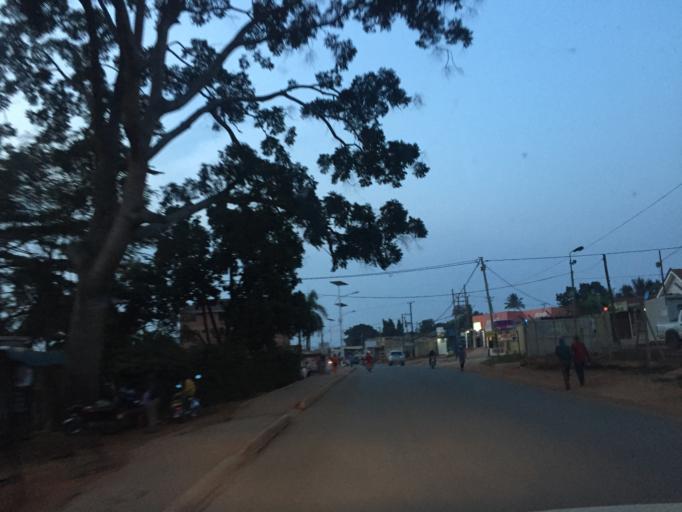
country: UG
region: Central Region
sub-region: Kampala District
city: Kampala
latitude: 0.3030
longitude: 32.6016
